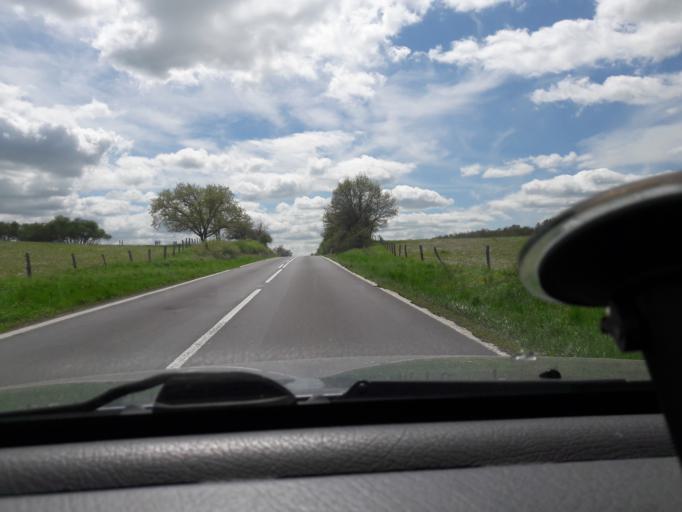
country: SK
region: Banskobystricky
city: Krupina
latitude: 48.3002
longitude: 19.0241
